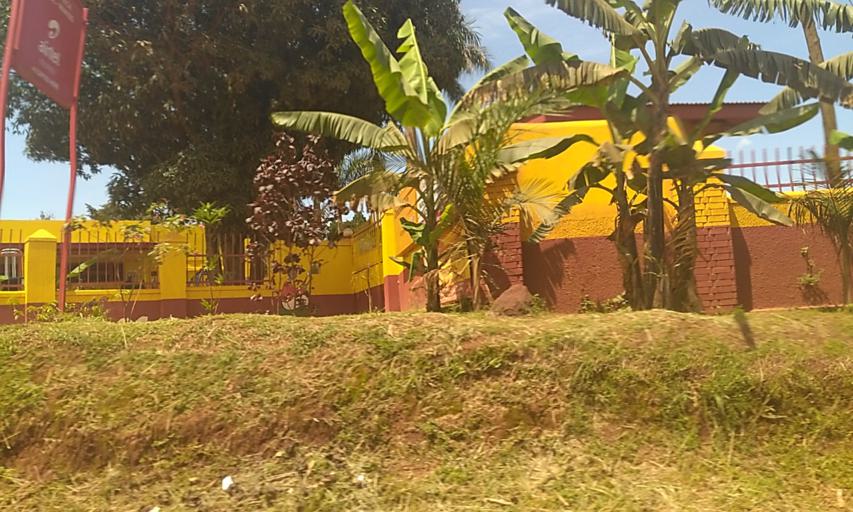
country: UG
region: Central Region
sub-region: Wakiso District
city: Wakiso
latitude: 0.4032
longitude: 32.4880
